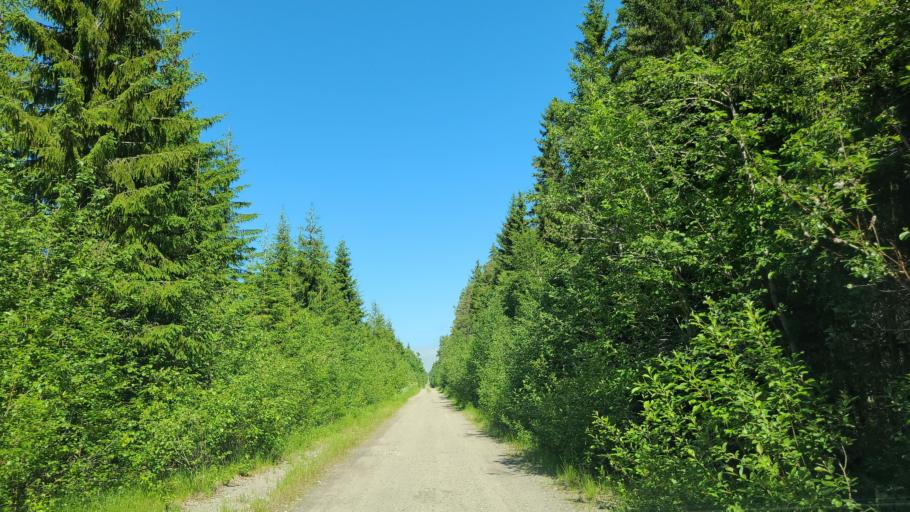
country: SE
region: Vaesternorrland
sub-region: OErnskoeldsviks Kommun
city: Husum
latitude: 63.4196
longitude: 19.2227
